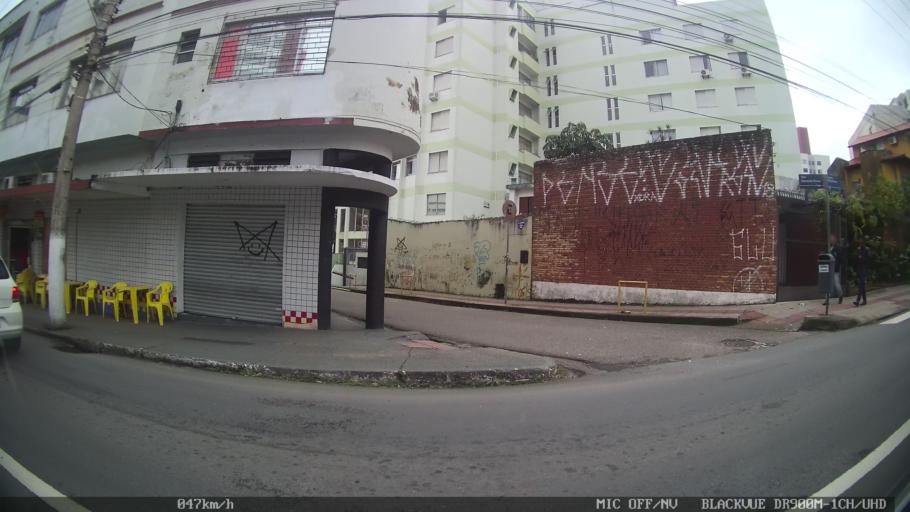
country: BR
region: Santa Catarina
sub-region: Florianopolis
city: Florianopolis
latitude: -27.5984
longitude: -48.5448
